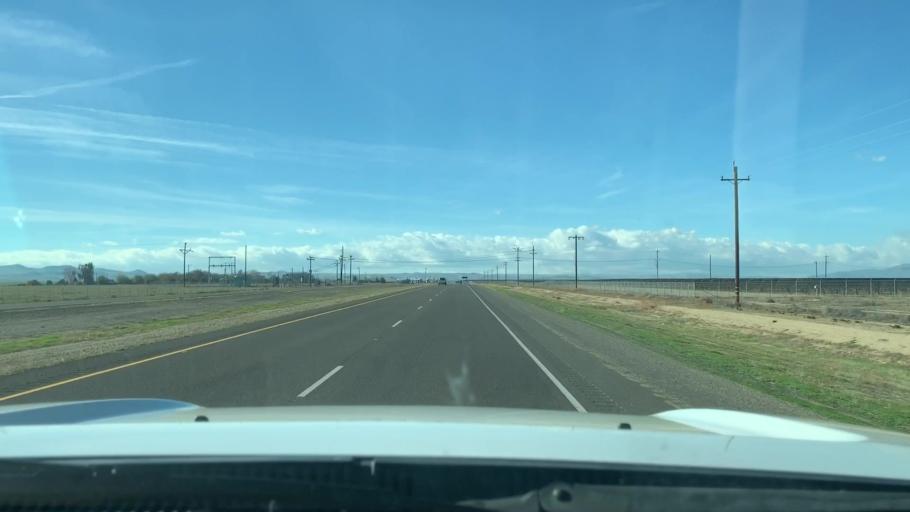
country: US
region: California
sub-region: Kern County
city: Lost Hills
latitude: 35.6154
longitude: -119.8503
